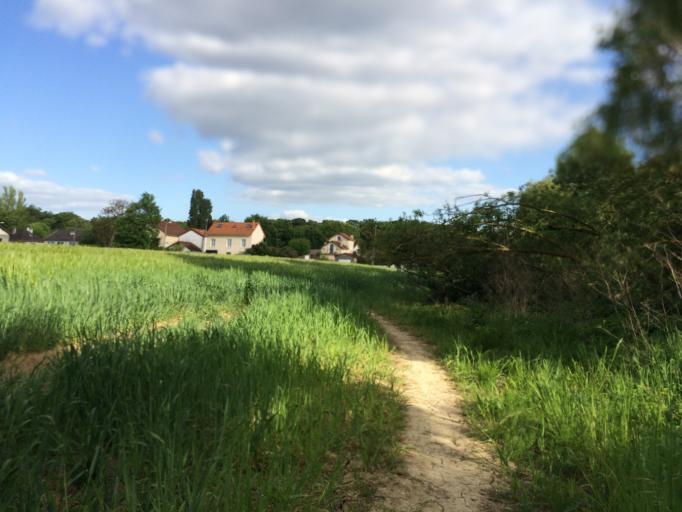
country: FR
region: Ile-de-France
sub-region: Departement de l'Essonne
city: Ris-Orangis
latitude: 48.6630
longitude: 2.4149
